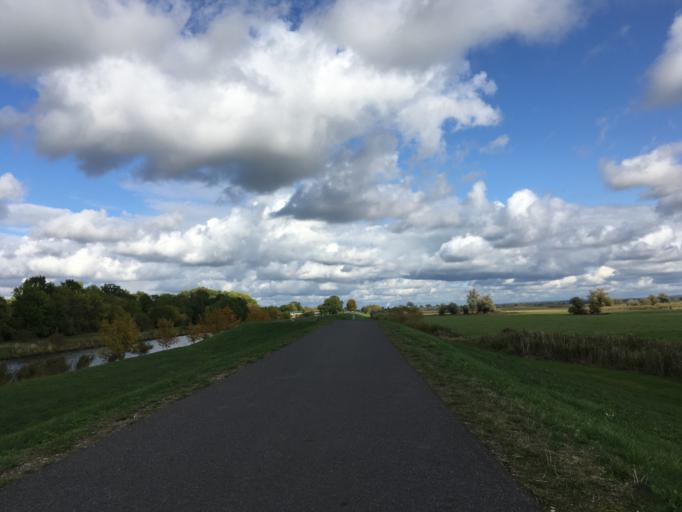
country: DE
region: Brandenburg
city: Meyenburg
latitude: 53.0199
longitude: 14.2406
